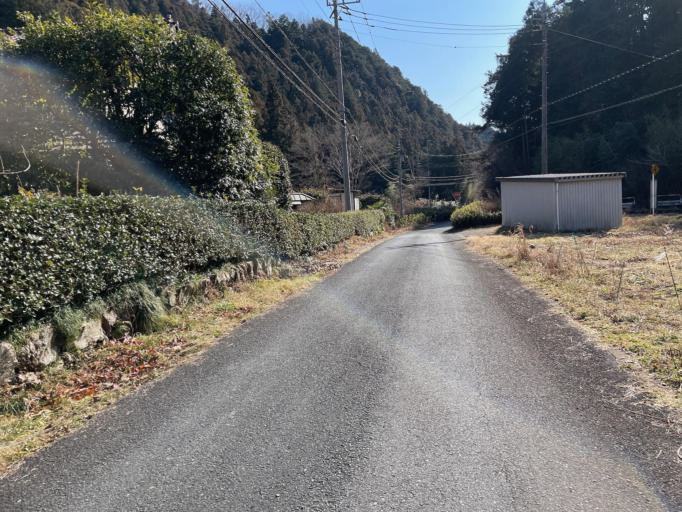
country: JP
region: Saitama
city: Hanno
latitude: 35.8494
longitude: 139.2550
